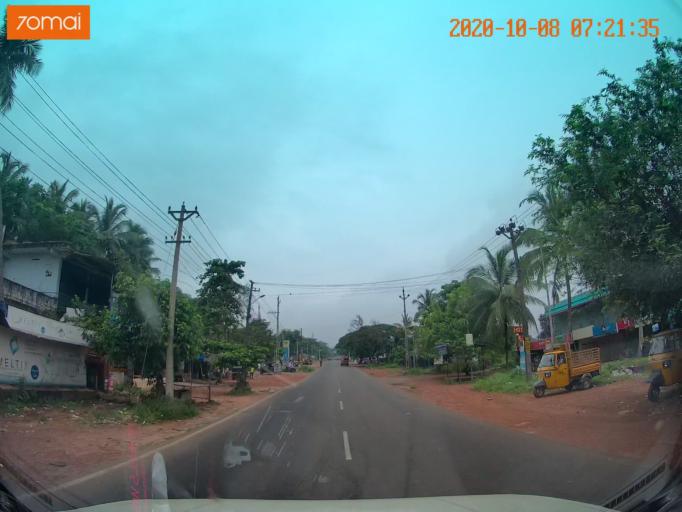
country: IN
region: Kerala
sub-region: Malappuram
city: Tirur
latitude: 10.8567
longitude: 76.0368
